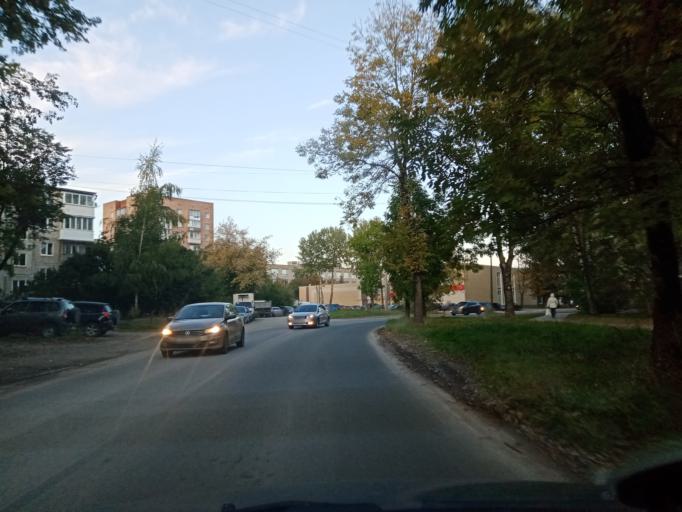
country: RU
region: Pskov
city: Pskov
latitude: 57.8060
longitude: 28.3427
